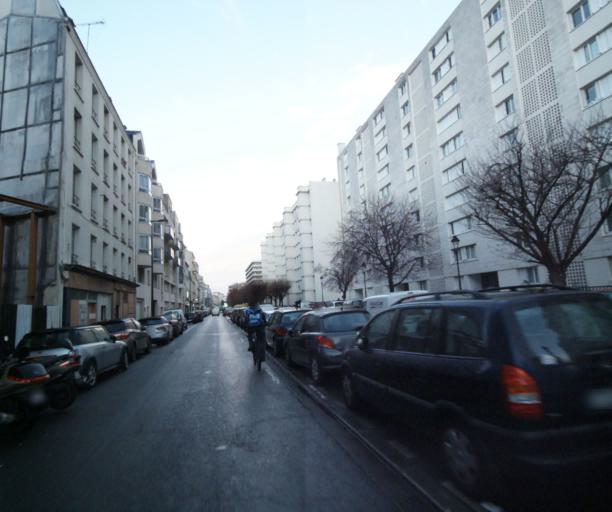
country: FR
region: Ile-de-France
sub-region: Departement des Hauts-de-Seine
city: Levallois-Perret
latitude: 48.8927
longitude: 2.2939
